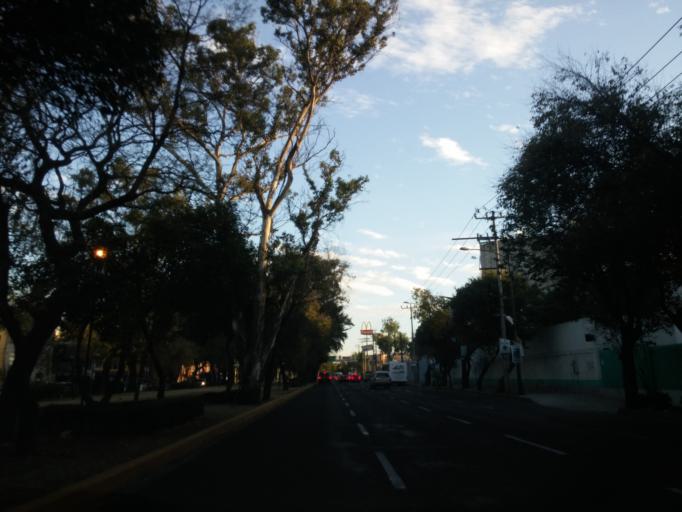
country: MX
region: Mexico City
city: Azcapotzalco
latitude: 19.4623
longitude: -99.1715
